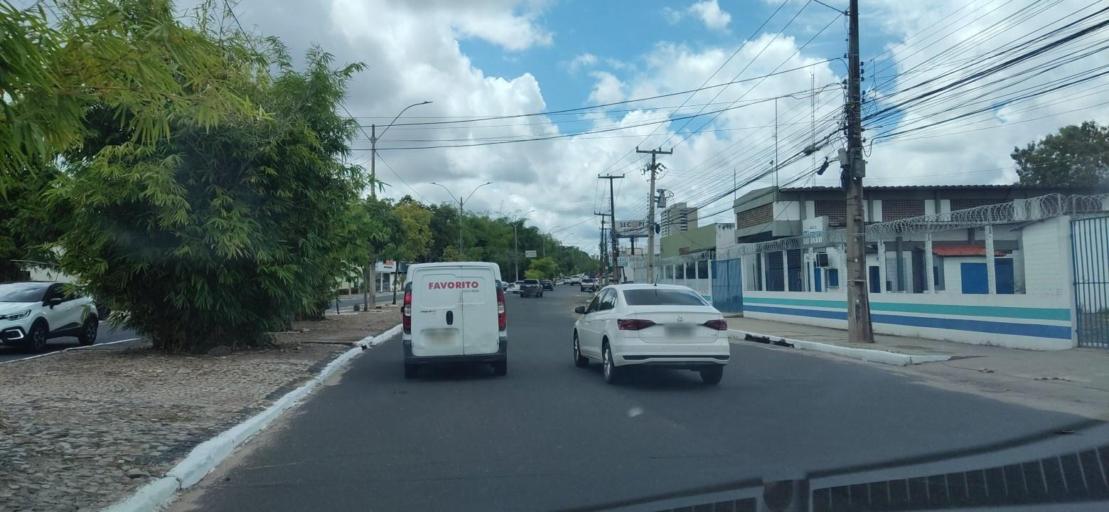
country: BR
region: Piaui
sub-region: Teresina
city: Teresina
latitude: -5.0621
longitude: -42.8033
